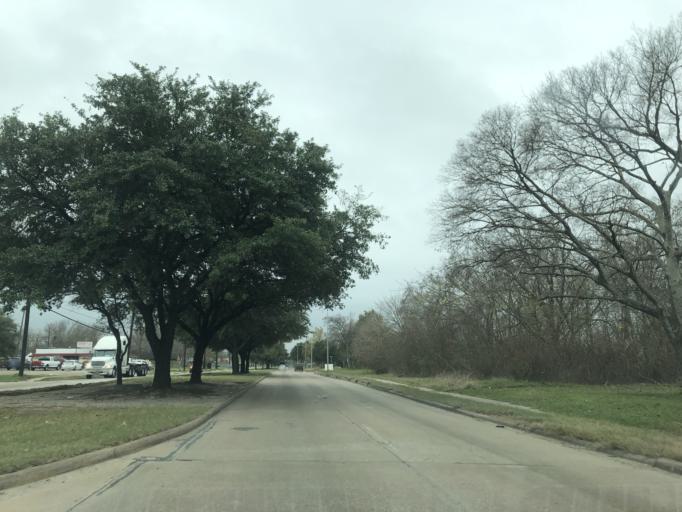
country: US
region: Texas
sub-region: Harris County
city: Jacinto City
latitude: 29.8198
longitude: -95.2846
